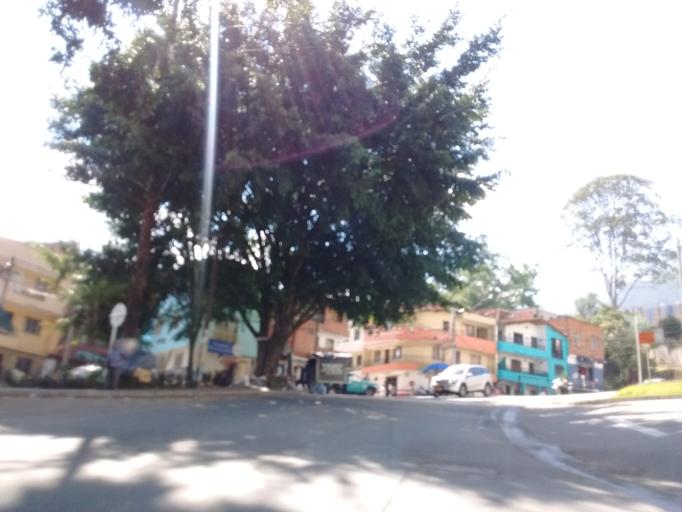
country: CO
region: Antioquia
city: Medellin
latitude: 6.2316
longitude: -75.5399
